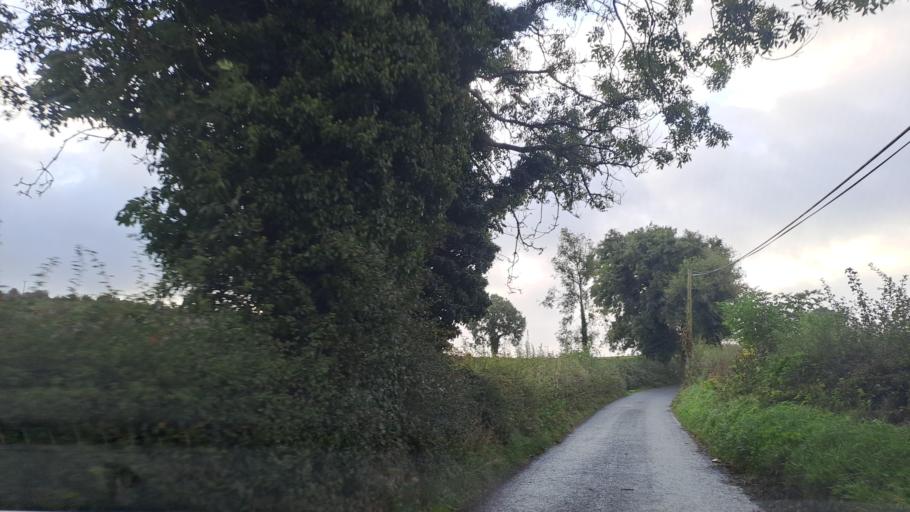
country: IE
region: Ulster
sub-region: An Cabhan
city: Kingscourt
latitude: 53.9699
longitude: -6.8435
